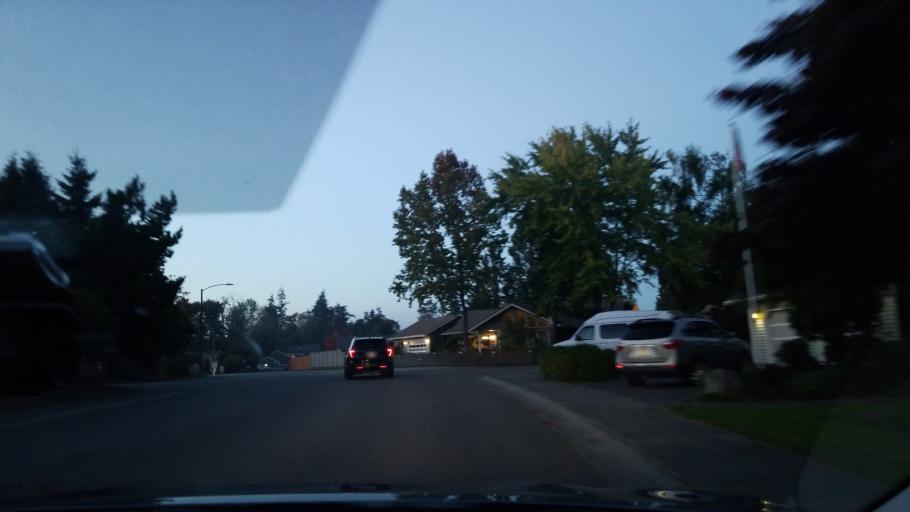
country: US
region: Washington
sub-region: Snohomish County
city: Silver Firs
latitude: 47.8782
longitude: -122.1731
